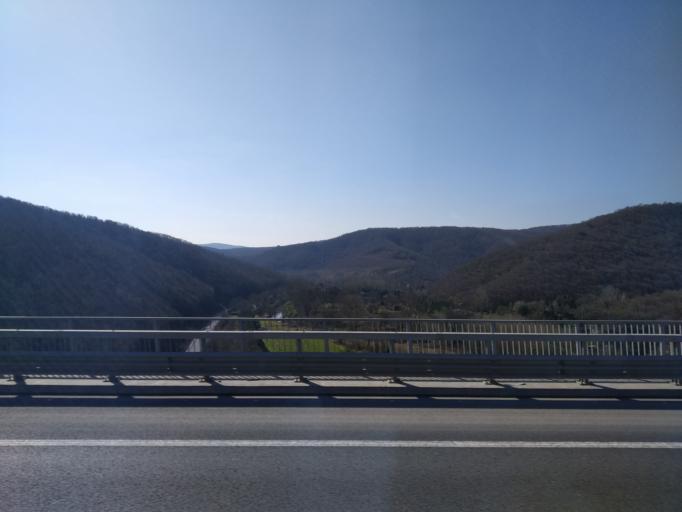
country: TR
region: Istanbul
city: Mahmut Sevket Pasa
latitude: 41.1529
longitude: 29.2683
